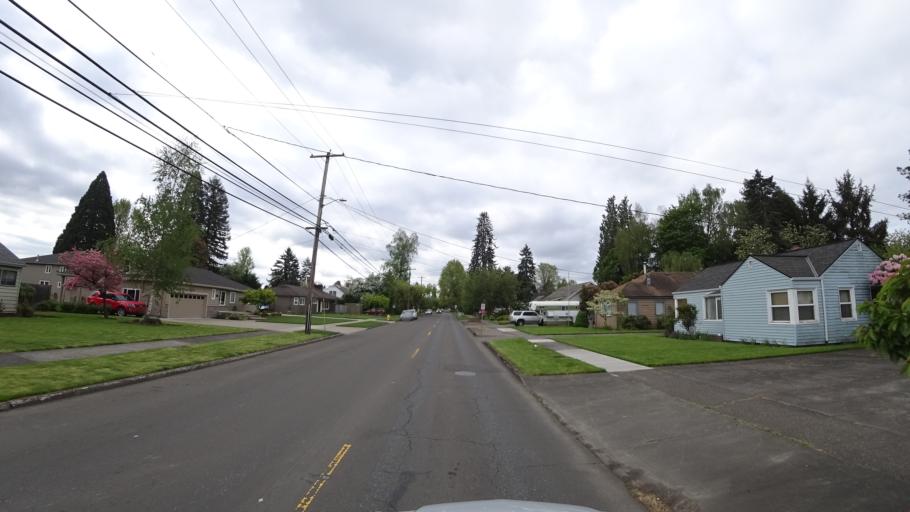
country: US
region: Oregon
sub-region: Washington County
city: Hillsboro
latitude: 45.5276
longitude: -122.9826
